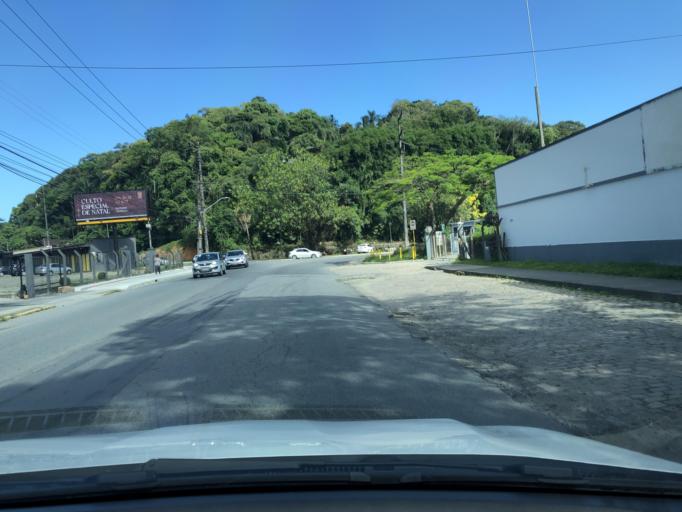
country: BR
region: Santa Catarina
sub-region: Joinville
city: Joinville
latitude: -26.3068
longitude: -48.8364
